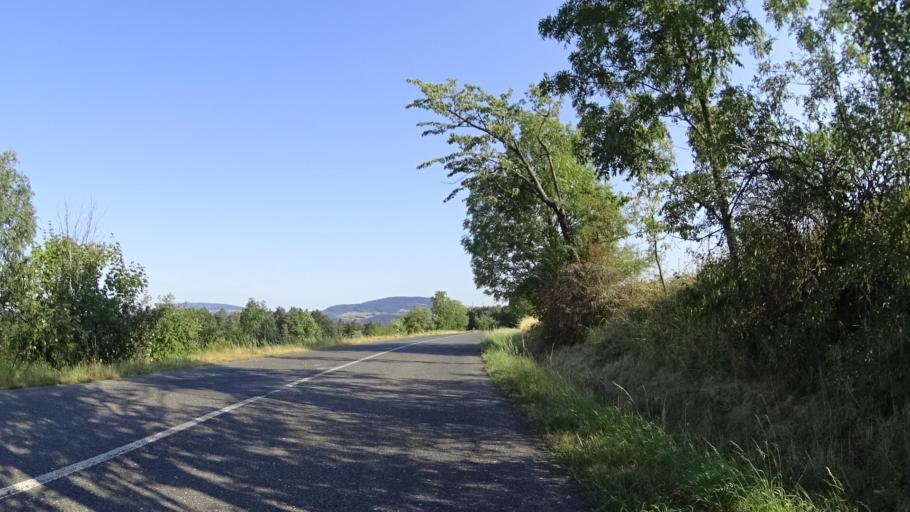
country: CZ
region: Liberecky
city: Hodkovice nad Mohelkou
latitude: 50.6460
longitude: 15.1061
